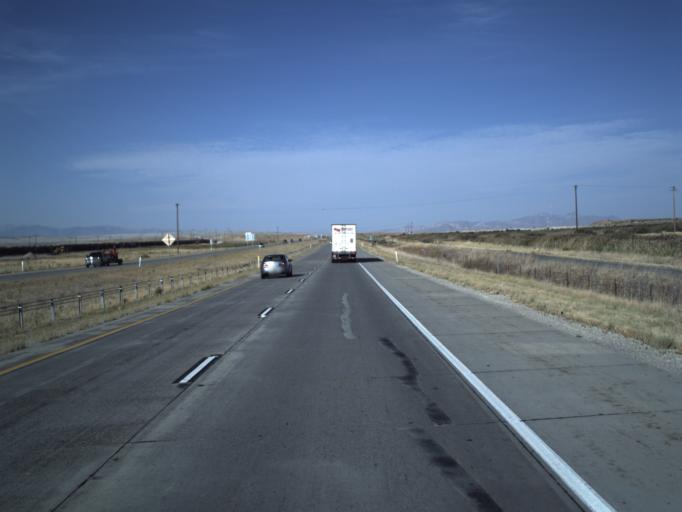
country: US
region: Utah
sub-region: Salt Lake County
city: Magna
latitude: 40.7712
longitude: -112.0460
